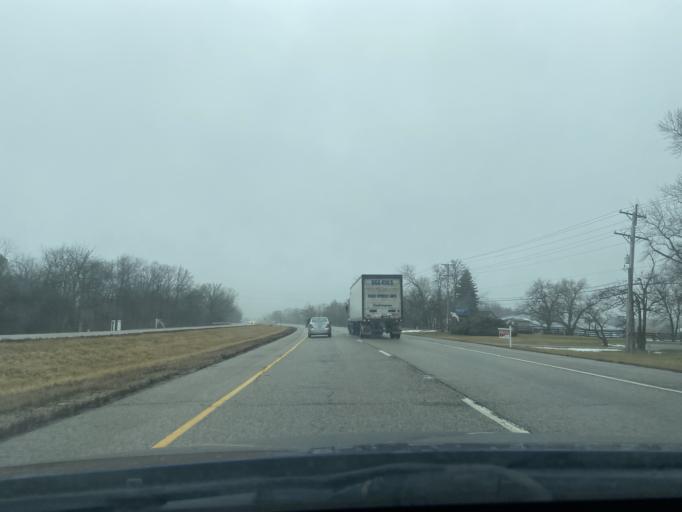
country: US
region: Illinois
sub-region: Lake County
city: Wauconda
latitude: 42.2402
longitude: -88.1150
